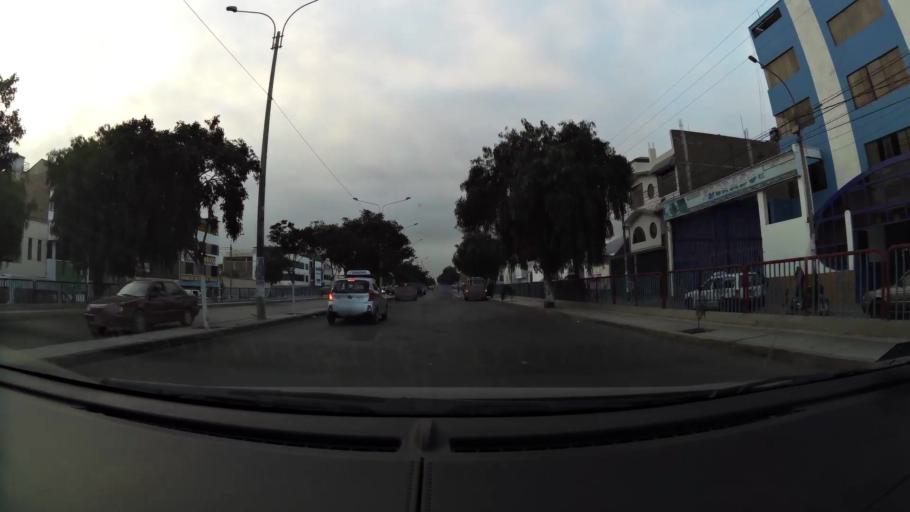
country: PE
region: La Libertad
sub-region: Provincia de Trujillo
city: Trujillo
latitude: -8.0998
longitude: -79.0369
